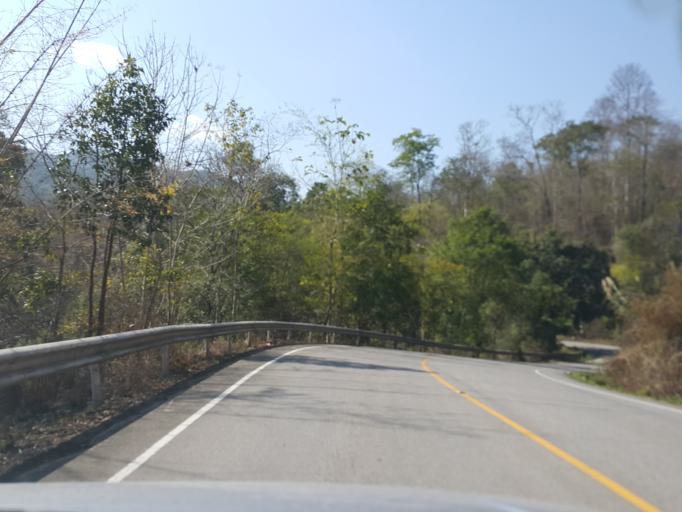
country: TH
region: Chiang Mai
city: Mae Wang
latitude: 18.6222
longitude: 98.7228
